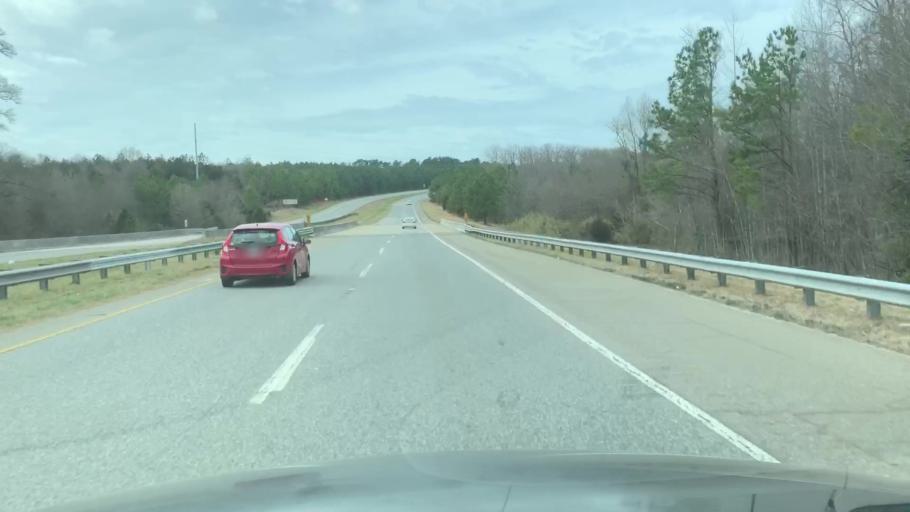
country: US
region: South Carolina
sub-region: Greenville County
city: Golden Grove
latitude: 34.7308
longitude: -82.4184
